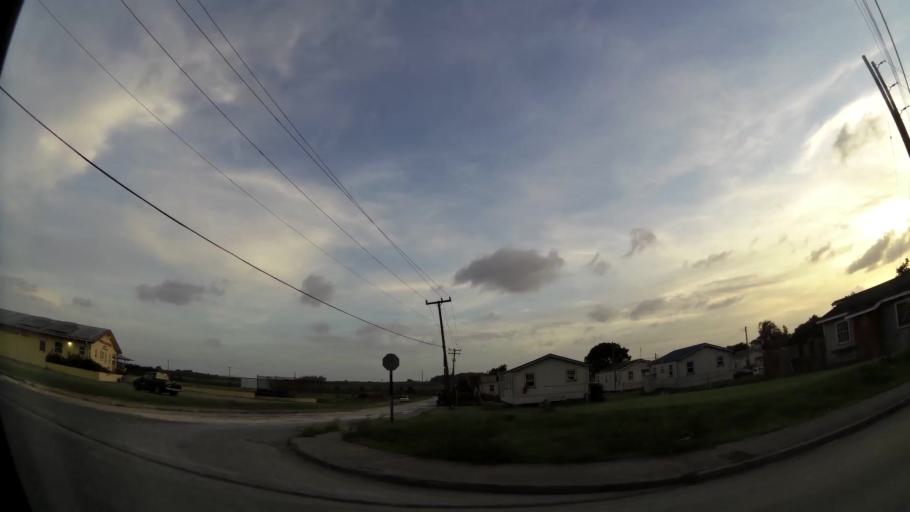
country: BB
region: Saint Philip
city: Crane
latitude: 13.1055
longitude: -59.4862
